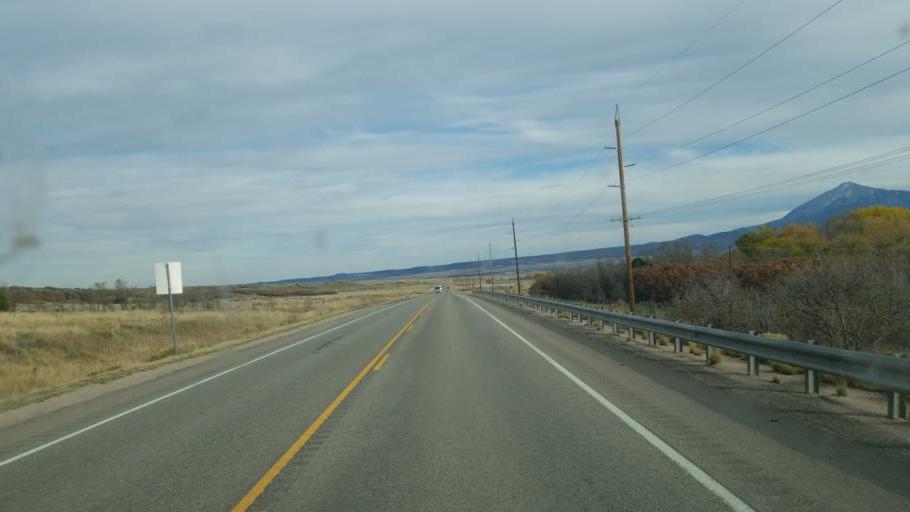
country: US
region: Colorado
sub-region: Huerfano County
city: Walsenburg
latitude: 37.5467
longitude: -105.0892
